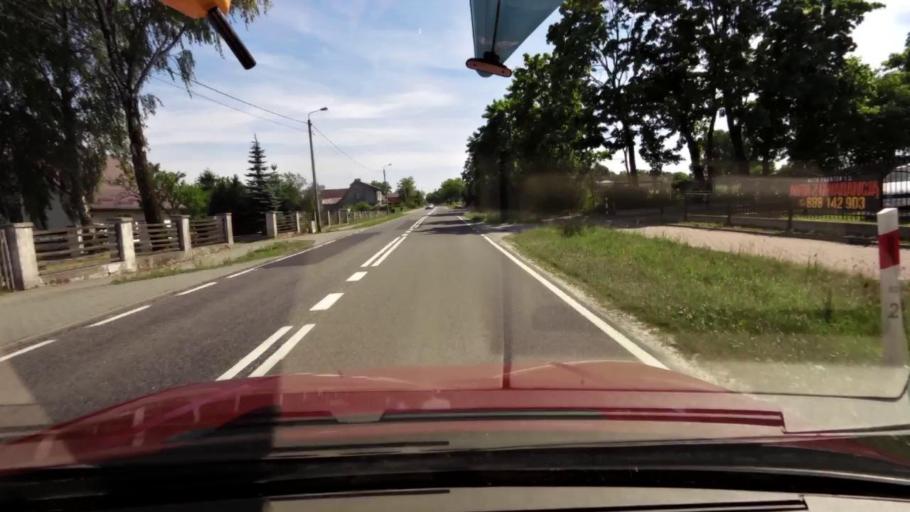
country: PL
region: Pomeranian Voivodeship
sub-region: Powiat slupski
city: Kobylnica
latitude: 54.4131
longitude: 17.0077
